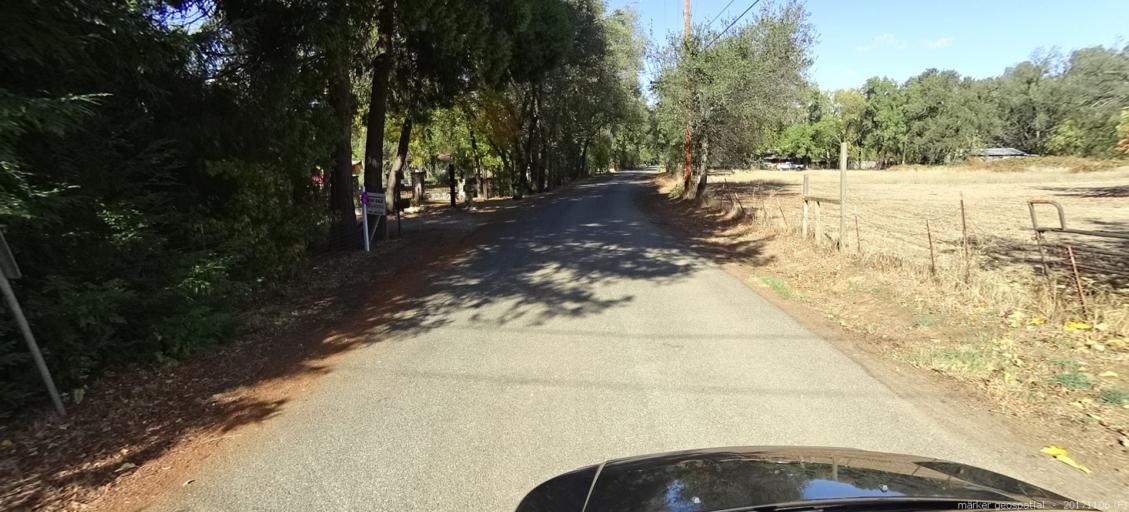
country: US
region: California
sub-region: Shasta County
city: Palo Cedro
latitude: 40.5818
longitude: -122.2958
